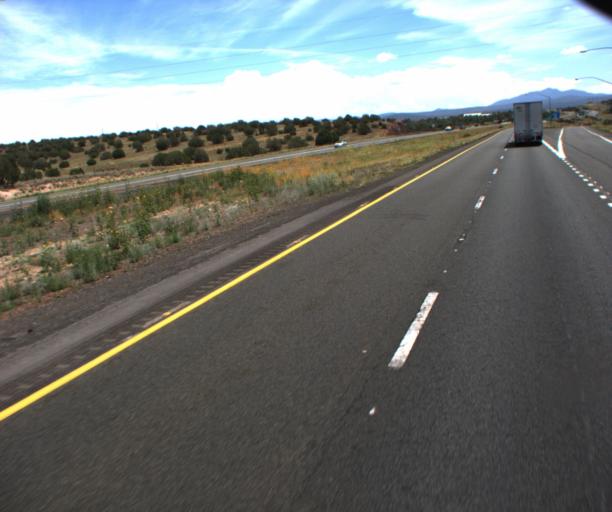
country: US
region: Arizona
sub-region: Coconino County
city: Williams
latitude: 35.2206
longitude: -112.5033
